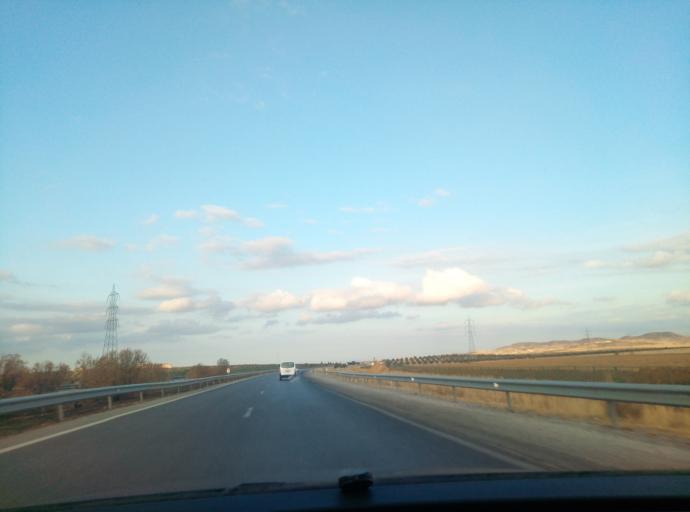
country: TN
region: Manouba
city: El Battan
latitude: 36.6652
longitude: 9.8598
